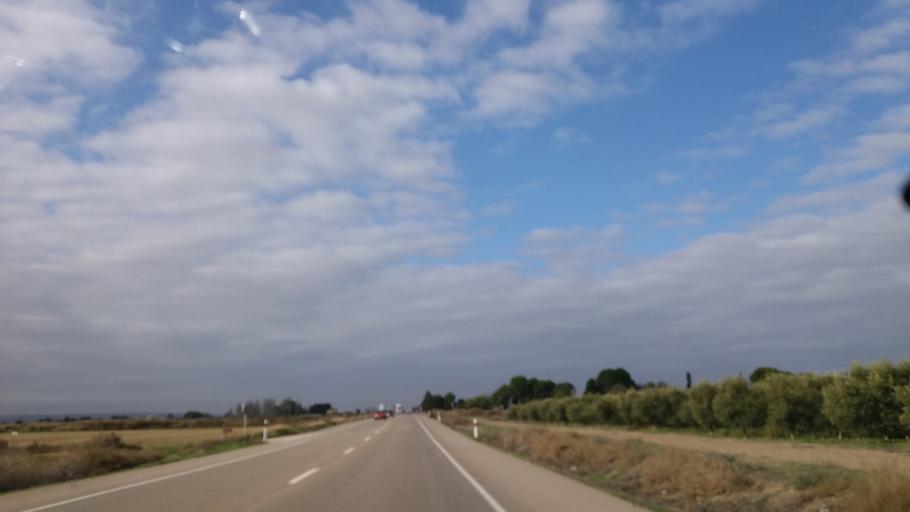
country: ES
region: Aragon
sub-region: Provincia de Zaragoza
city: Pina de Ebro
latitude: 41.5278
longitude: -0.5519
